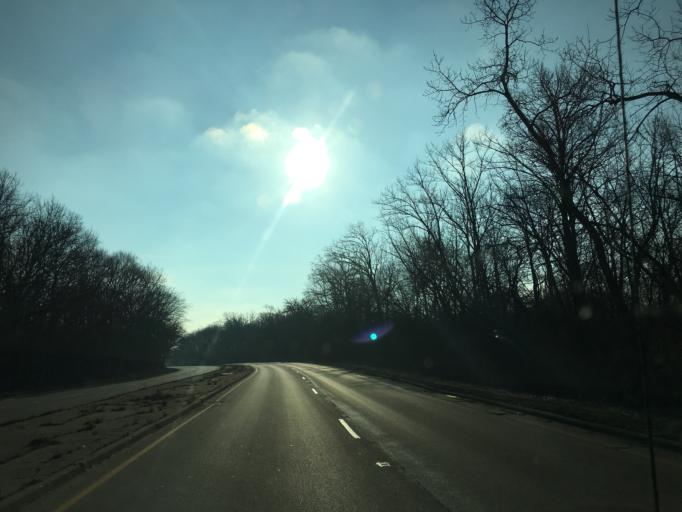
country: US
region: Illinois
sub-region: Cook County
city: Elk Grove Village
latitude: 42.0294
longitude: -87.9957
